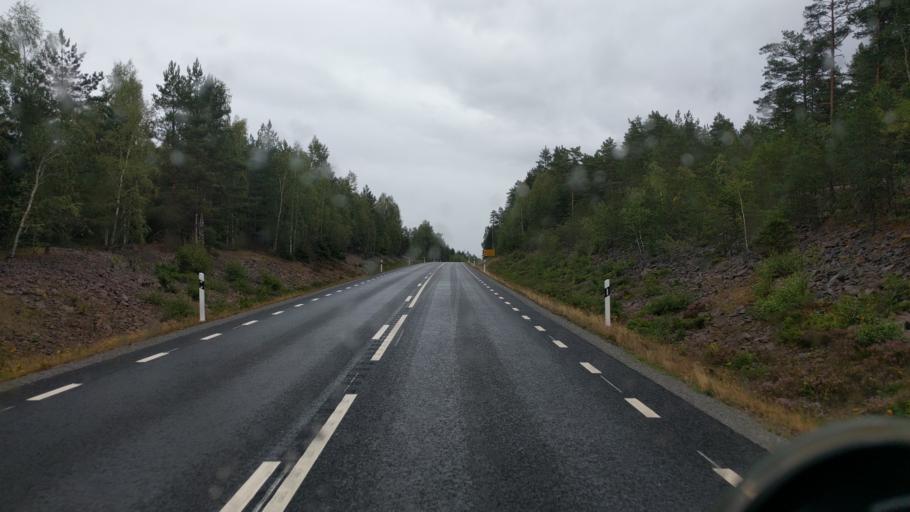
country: SE
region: Kalmar
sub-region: Vasterviks Kommun
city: Ankarsrum
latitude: 57.7127
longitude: 16.3376
